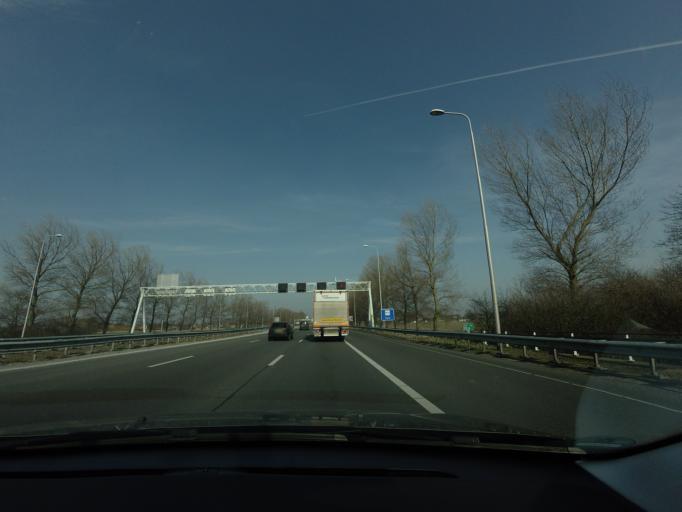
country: NL
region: North Holland
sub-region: Gemeente Uitgeest
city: Uitgeest
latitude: 52.5223
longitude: 4.7194
